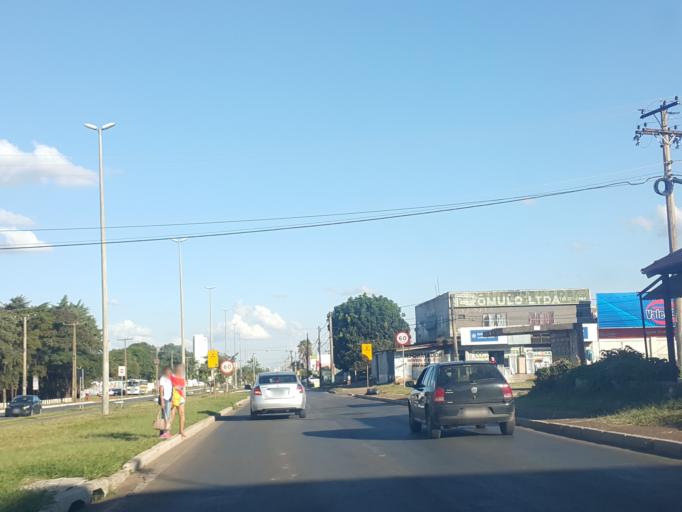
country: BR
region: Federal District
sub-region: Brasilia
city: Brasilia
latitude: -15.8223
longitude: -48.0945
